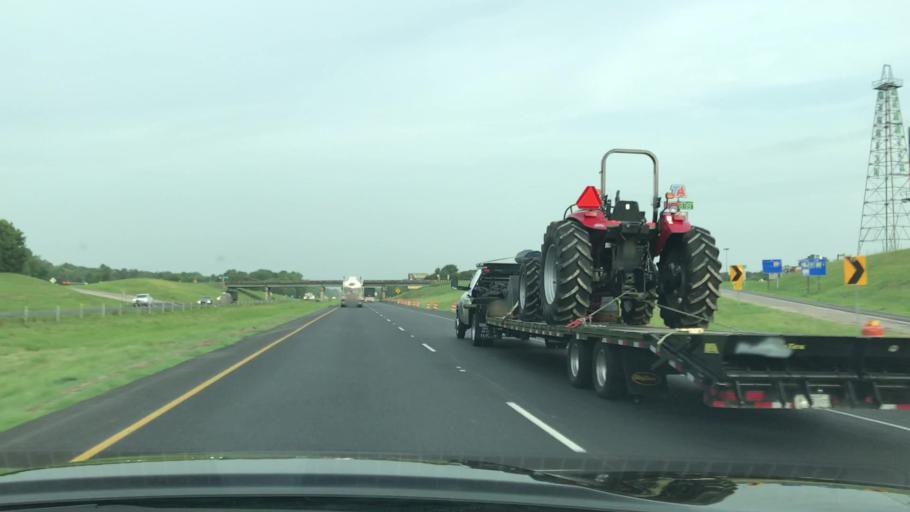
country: US
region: Louisiana
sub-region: Caddo Parish
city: Greenwood
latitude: 32.4440
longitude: -93.9463
